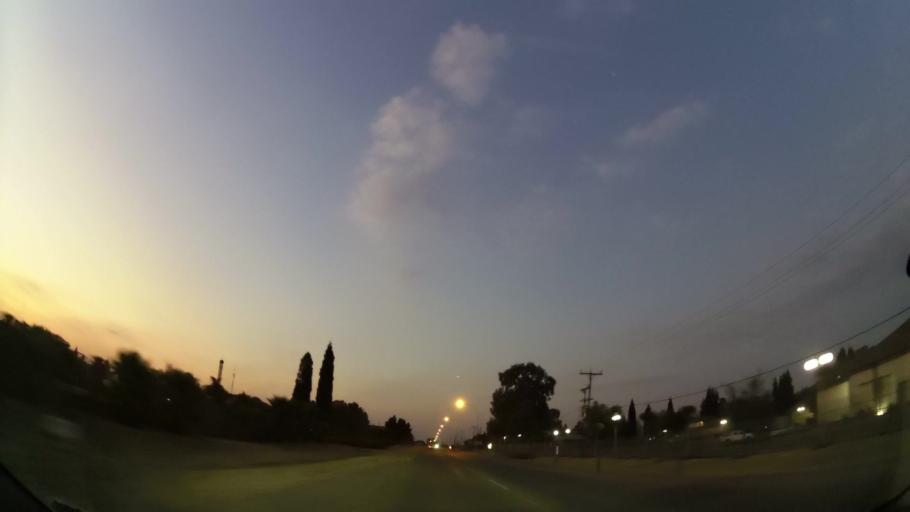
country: ZA
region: Gauteng
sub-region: Ekurhuleni Metropolitan Municipality
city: Benoni
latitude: -26.1068
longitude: 28.3194
